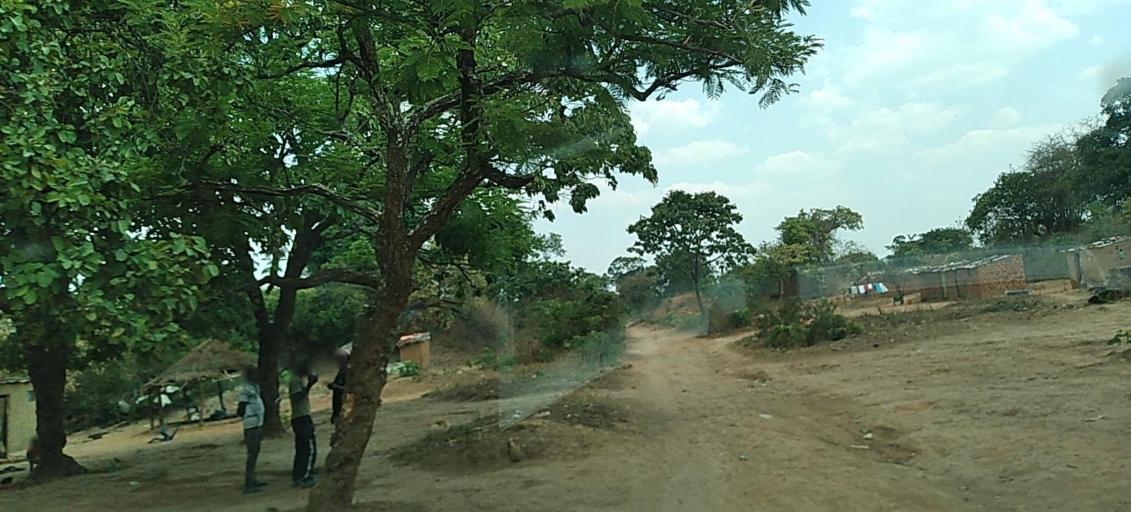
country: CD
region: Katanga
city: Kipushi
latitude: -12.0277
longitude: 27.4356
